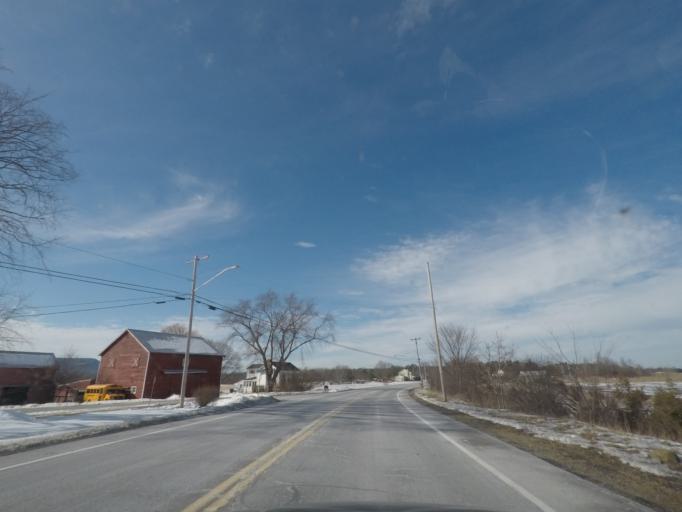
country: US
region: New York
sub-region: Albany County
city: Voorheesville
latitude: 42.6800
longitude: -73.9623
